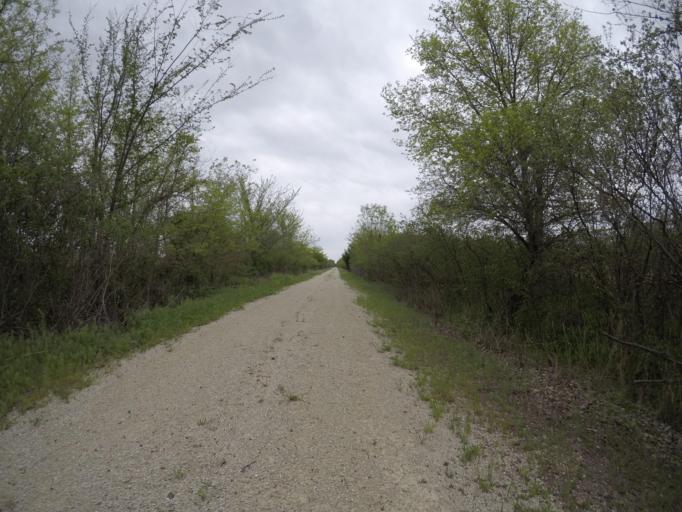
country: US
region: Nebraska
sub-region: Gage County
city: Wymore
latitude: 40.1022
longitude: -96.6109
